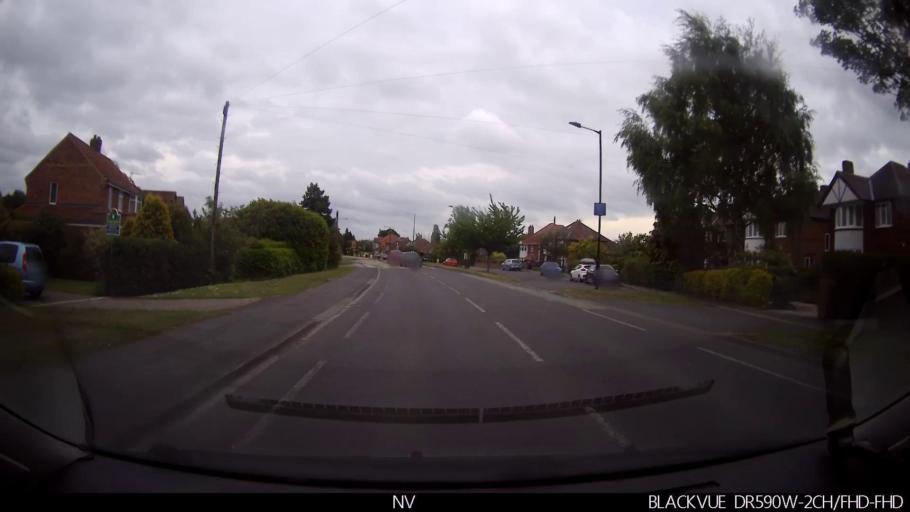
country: GB
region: England
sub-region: City of York
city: Haxby
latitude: 54.0069
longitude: -1.0742
